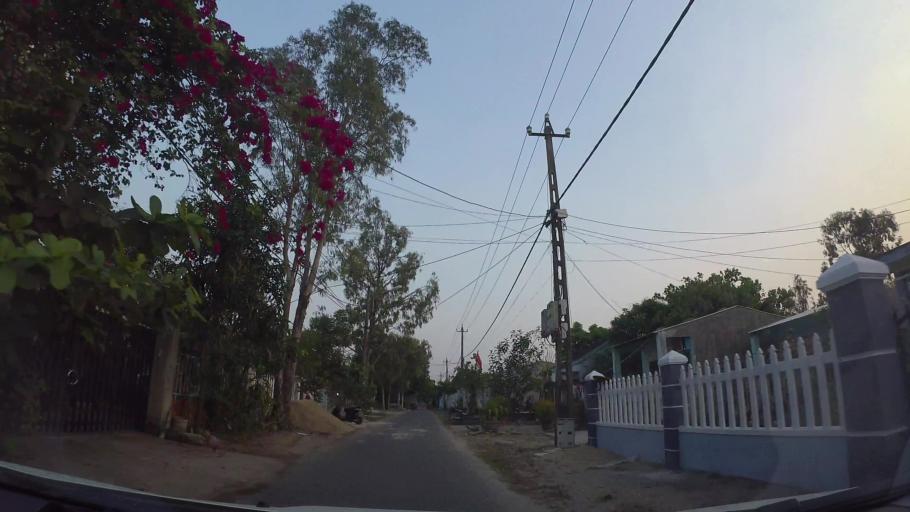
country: VN
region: Da Nang
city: Ngu Hanh Son
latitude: 15.9741
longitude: 108.2399
